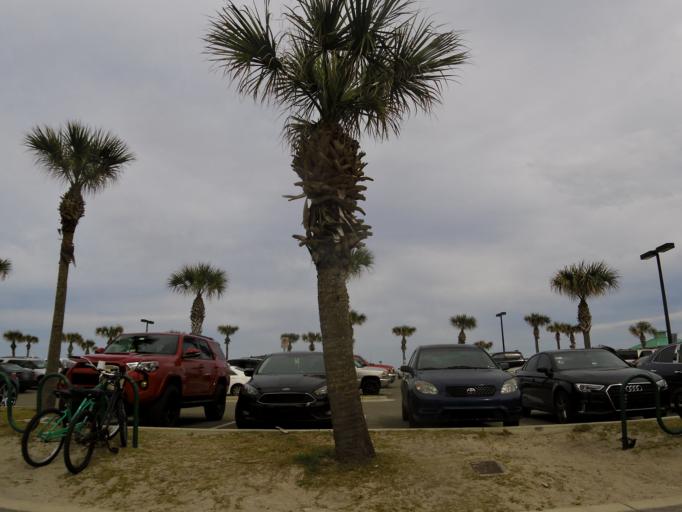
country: US
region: Florida
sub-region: Duval County
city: Jacksonville Beach
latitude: 30.2937
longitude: -81.3905
